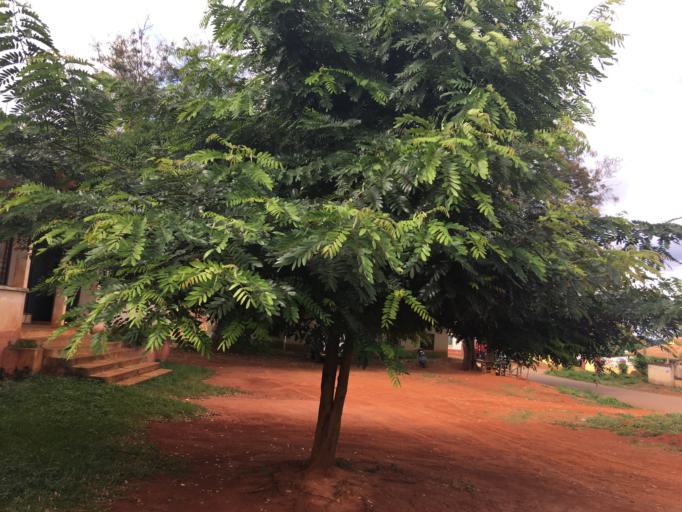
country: GH
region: Western
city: Bibiani
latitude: 6.8083
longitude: -2.5167
